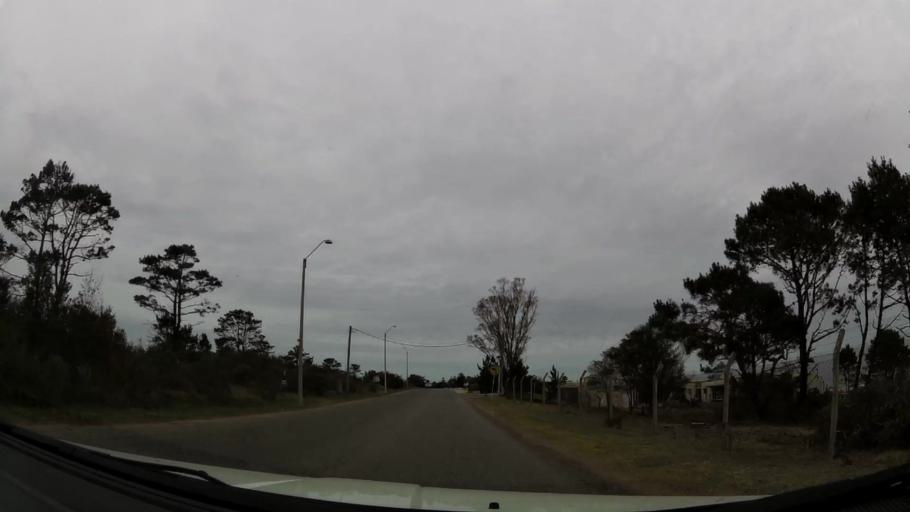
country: UY
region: Maldonado
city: Maldonado
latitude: -34.9010
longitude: -55.0401
